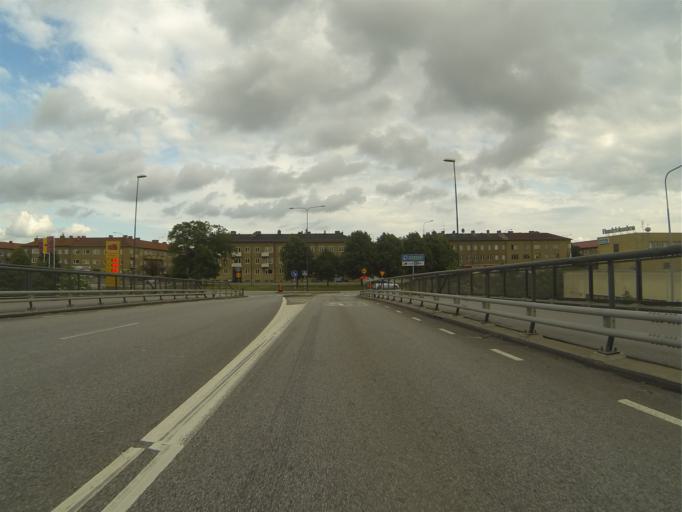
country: SE
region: Skane
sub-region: Burlovs Kommun
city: Arloev
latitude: 55.6154
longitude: 13.0416
